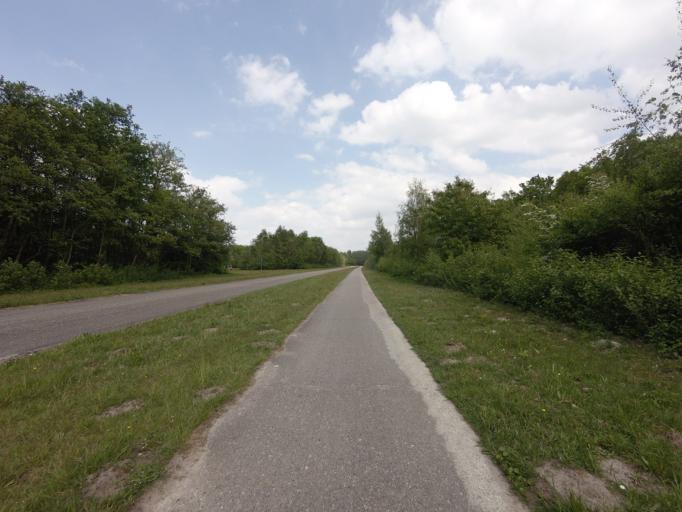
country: NL
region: Zeeland
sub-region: Schouwen-Duiveland
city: Bruinisse
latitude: 51.6751
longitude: 4.1085
